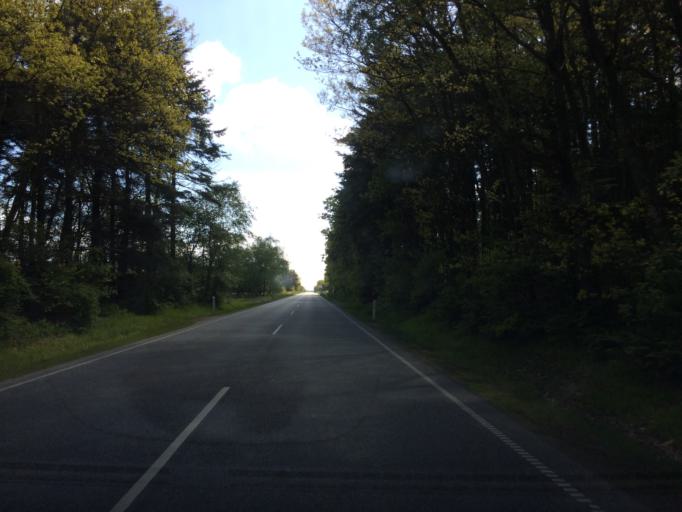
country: DK
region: Central Jutland
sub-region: Holstebro Kommune
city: Ulfborg
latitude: 56.2845
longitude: 8.1798
